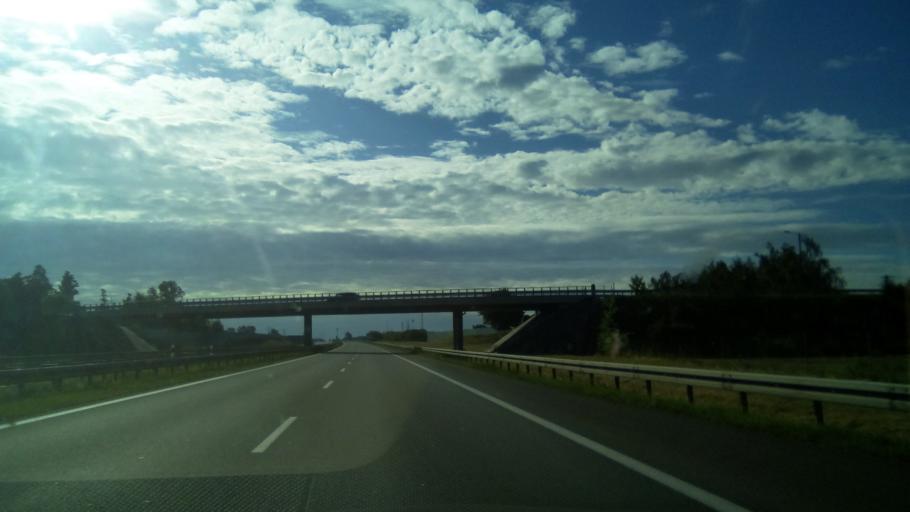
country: PL
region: Greater Poland Voivodeship
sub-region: Powiat koninski
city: Golina
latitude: 52.1828
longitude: 18.1029
